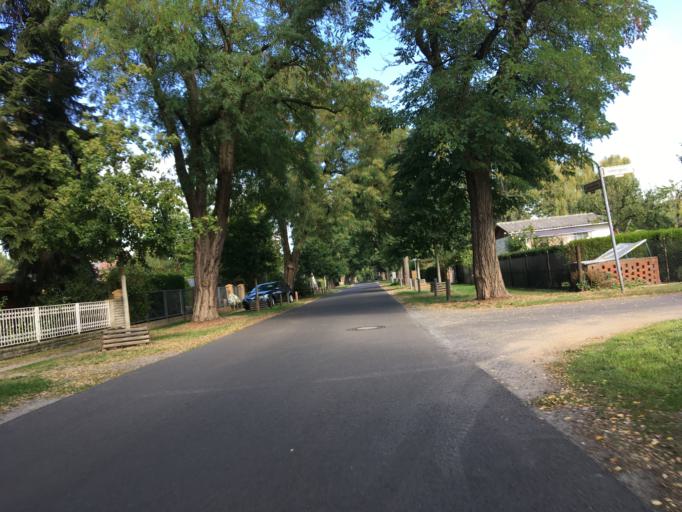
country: DE
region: Berlin
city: Kaulsdorf
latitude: 52.5238
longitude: 13.5975
